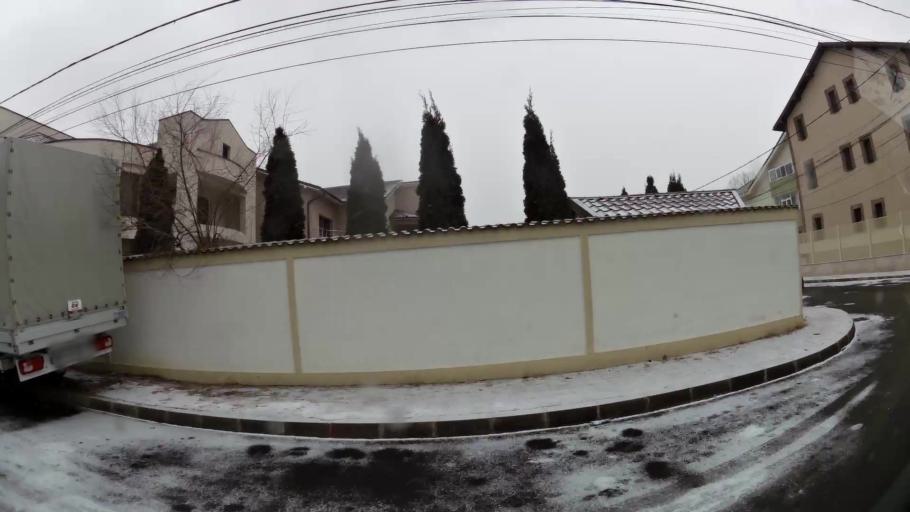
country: RO
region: Dambovita
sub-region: Municipiul Targoviste
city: Targoviste
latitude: 44.9308
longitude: 25.4441
